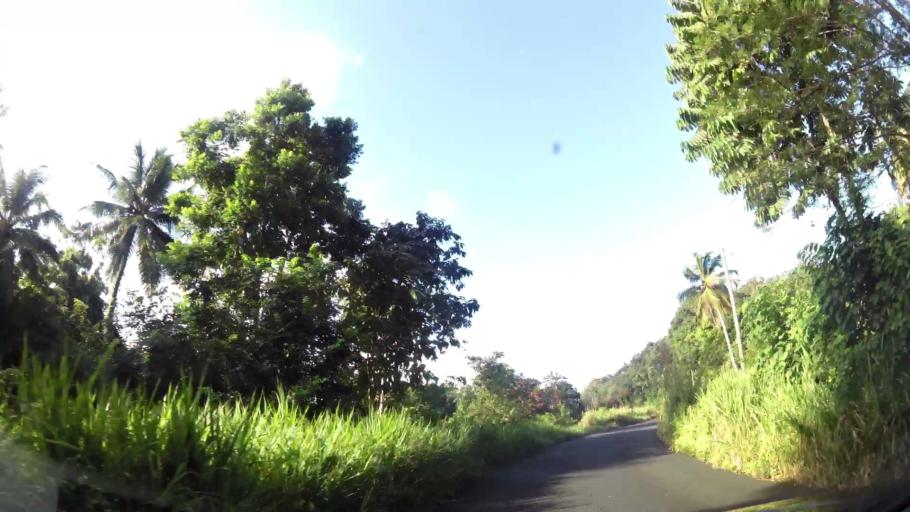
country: DM
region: Saint Andrew
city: Calibishie
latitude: 15.5946
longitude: -61.3650
